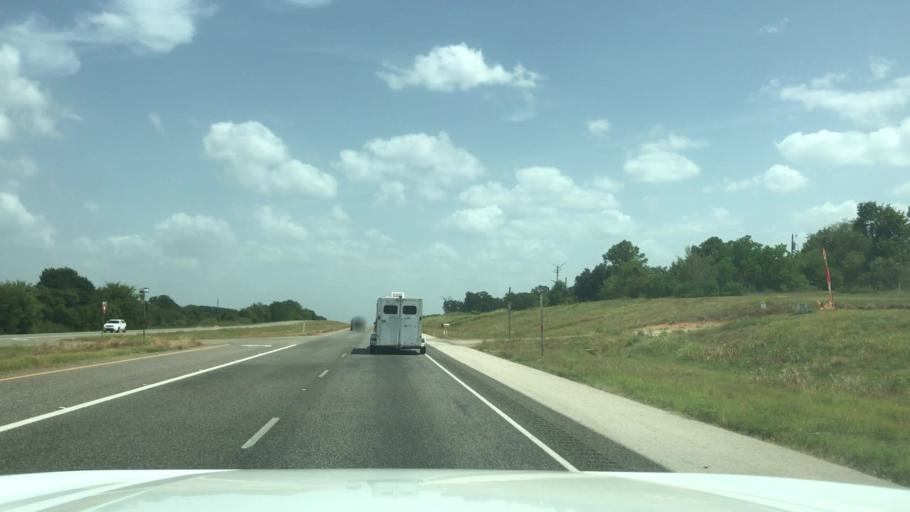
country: US
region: Texas
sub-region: Robertson County
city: Hearne
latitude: 30.9276
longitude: -96.6302
